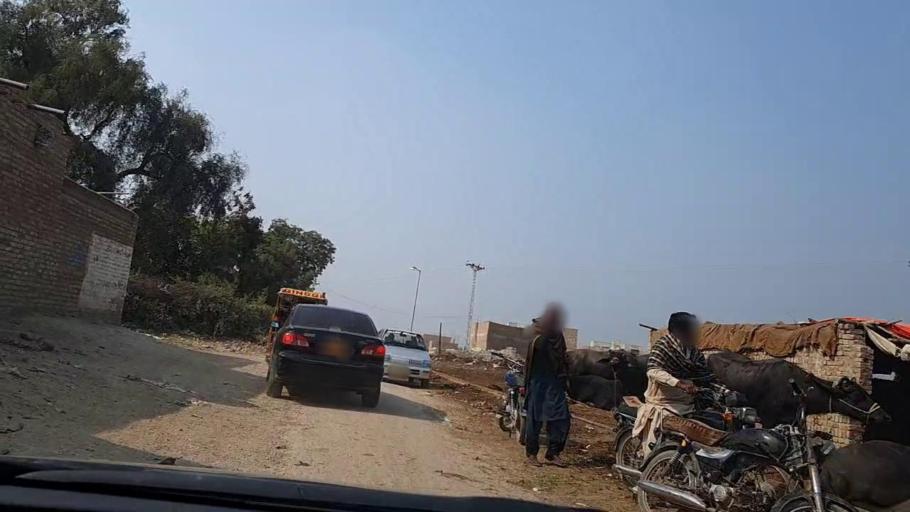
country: PK
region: Sindh
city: Sakrand
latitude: 26.1444
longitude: 68.2692
